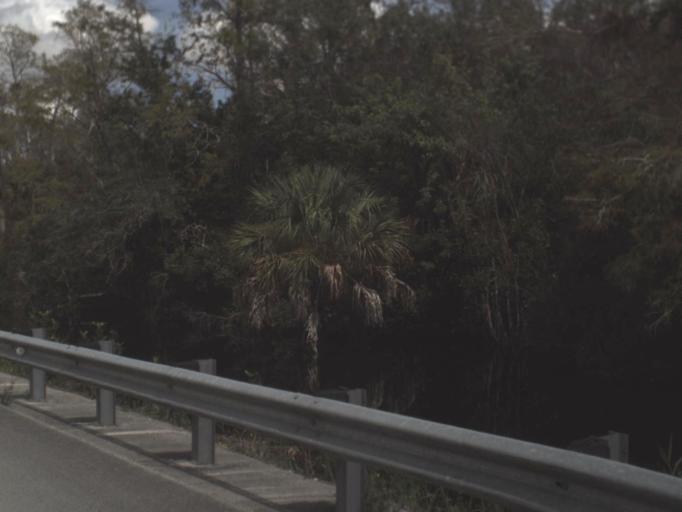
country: US
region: Florida
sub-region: Collier County
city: Lely Resort
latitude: 25.9387
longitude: -81.3572
